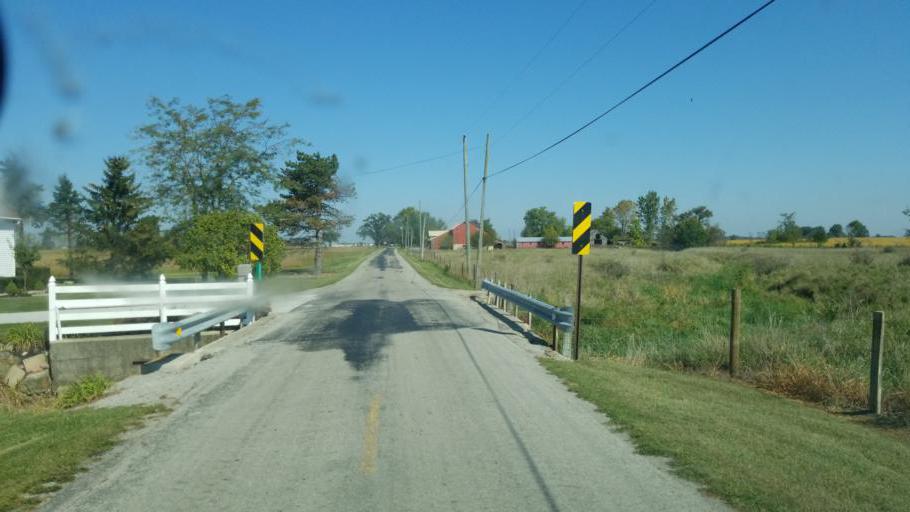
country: US
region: Ohio
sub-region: Union County
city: Richwood
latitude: 40.5090
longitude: -83.4373
